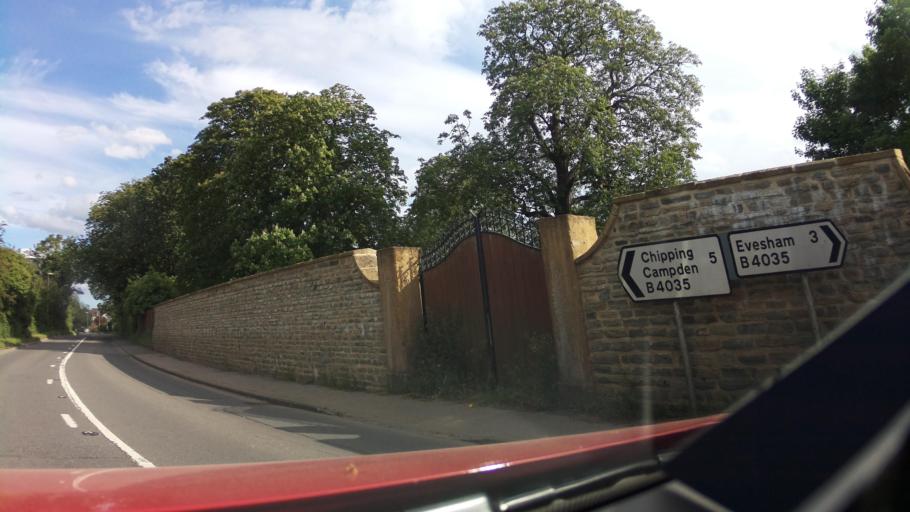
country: GB
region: England
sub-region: Worcestershire
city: South Littleton
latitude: 52.0952
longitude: -1.8669
